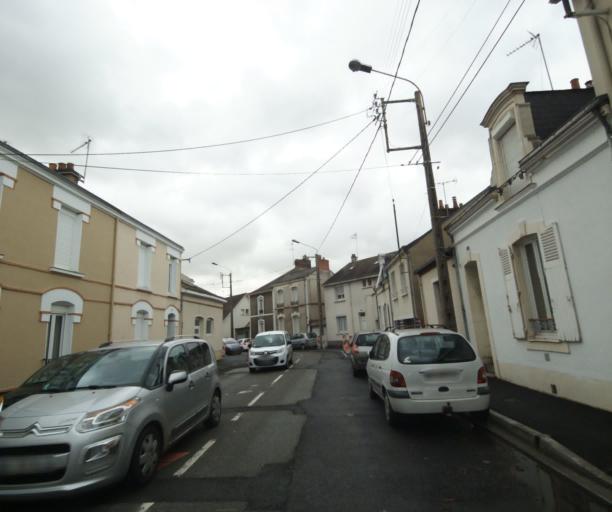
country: FR
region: Pays de la Loire
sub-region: Departement de la Sarthe
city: Le Mans
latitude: 48.0028
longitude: 0.1786
